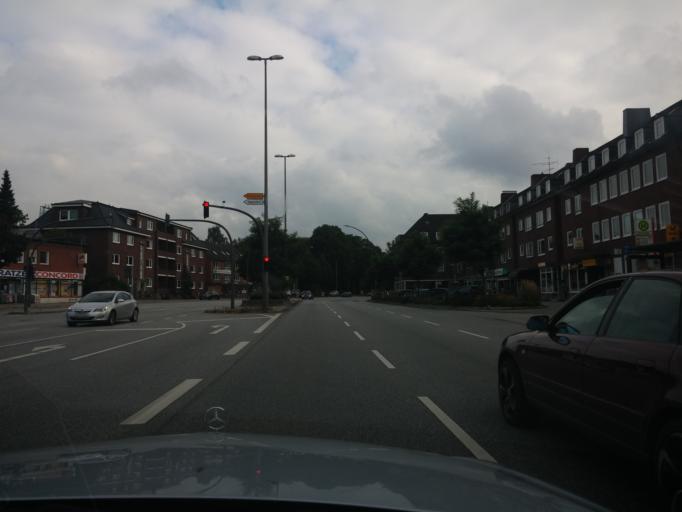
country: DE
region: Hamburg
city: Hamburg-Nord
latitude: 53.5995
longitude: 9.9642
